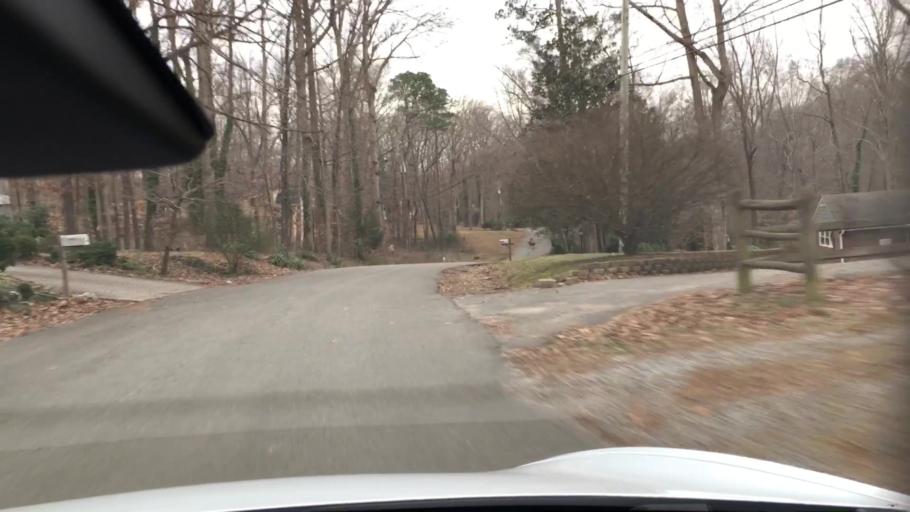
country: US
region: Virginia
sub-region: Chesterfield County
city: Bon Air
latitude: 37.5298
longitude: -77.5662
